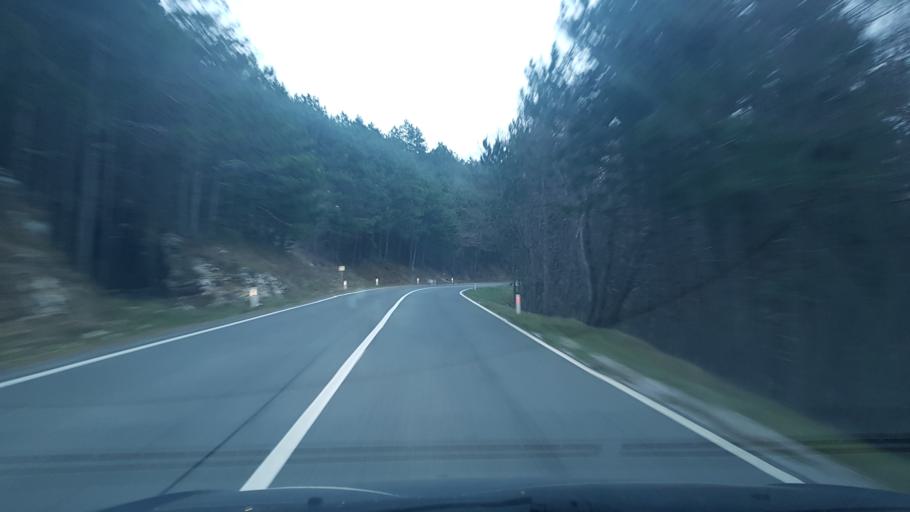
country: SI
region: Vipava
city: Vipava
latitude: 45.8802
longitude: 13.9559
